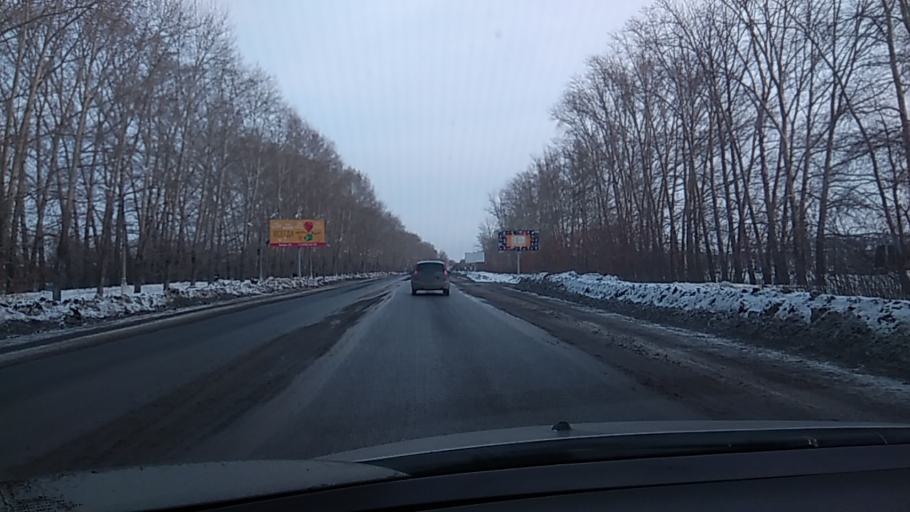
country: RU
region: Sverdlovsk
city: Martyush
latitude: 56.4395
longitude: 61.8365
